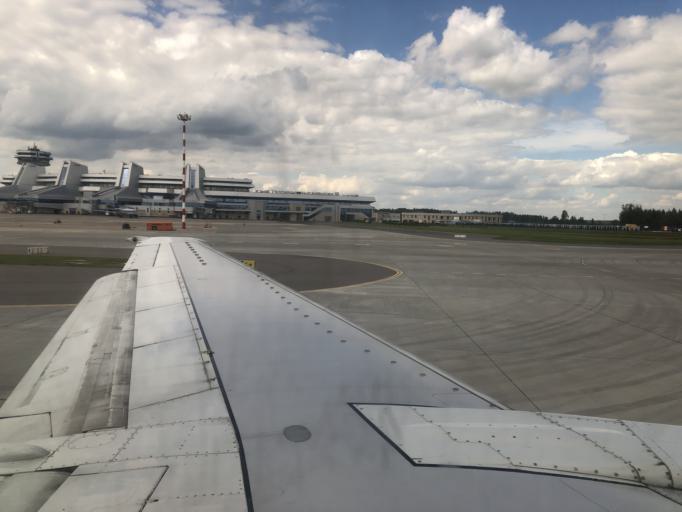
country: BY
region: Minsk
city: Smilavichy
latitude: 53.8880
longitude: 28.0405
